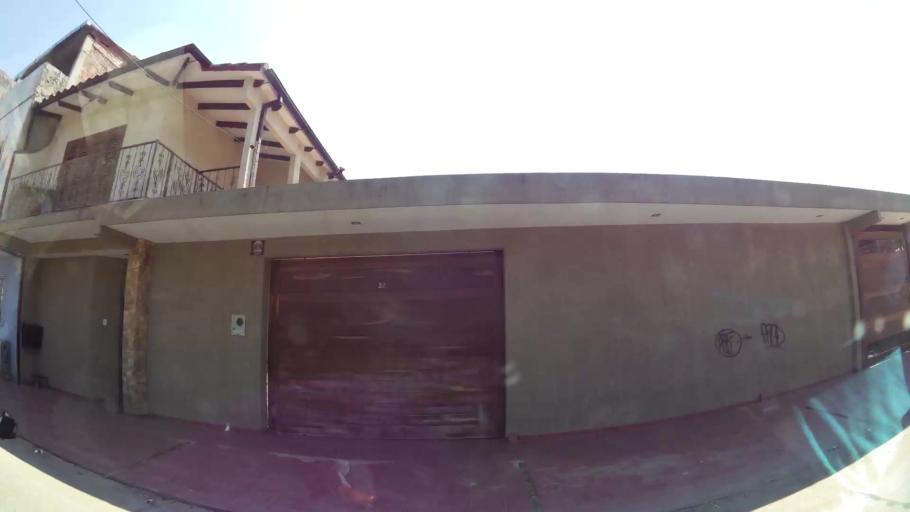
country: BO
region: Santa Cruz
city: Santa Cruz de la Sierra
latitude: -17.7438
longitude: -63.1790
